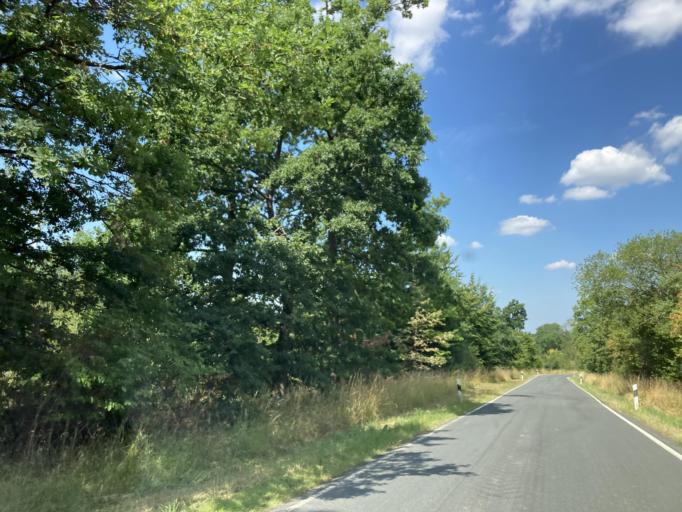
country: DE
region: Hesse
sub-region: Regierungsbezirk Giessen
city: Lauterbach
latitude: 50.5896
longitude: 9.3967
